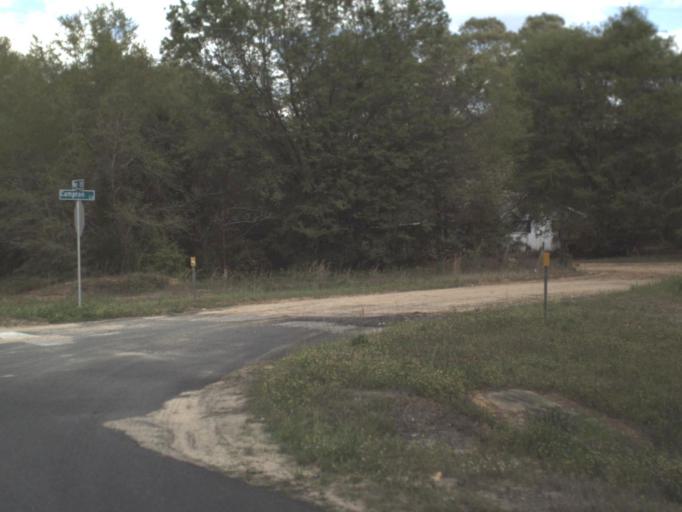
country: US
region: Florida
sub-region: Okaloosa County
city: Crestview
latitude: 30.8736
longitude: -86.5188
